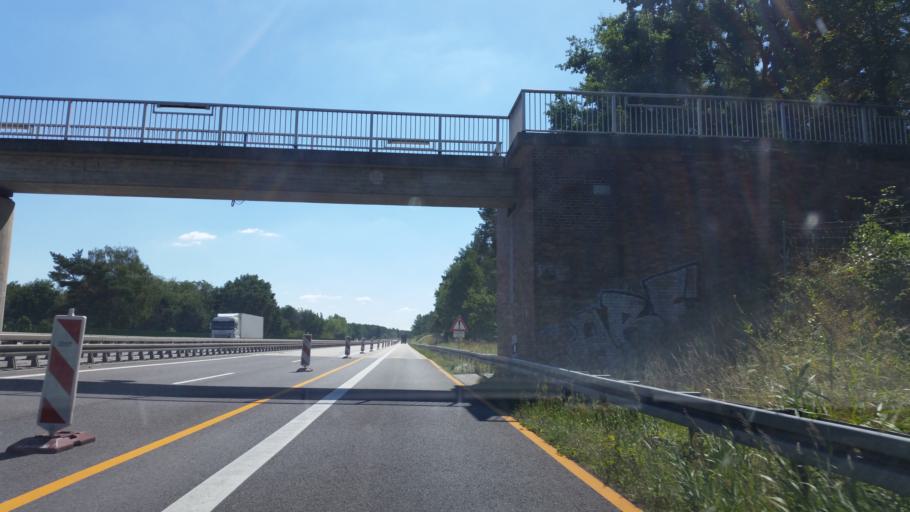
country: DE
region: Brandenburg
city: Vetschau
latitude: 51.7744
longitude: 14.0858
